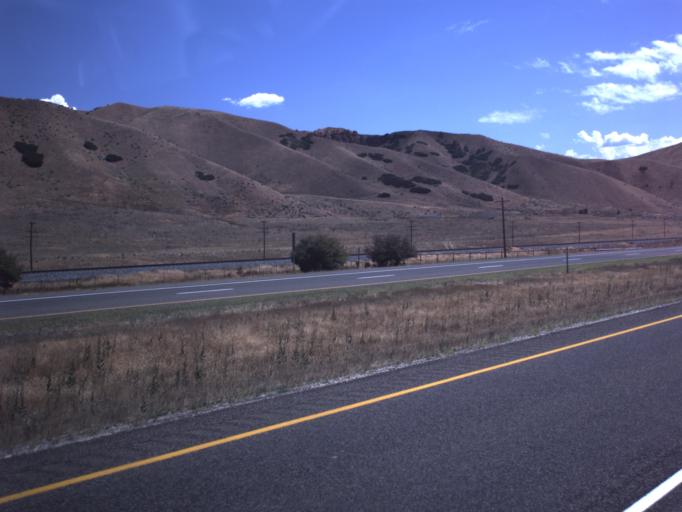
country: US
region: Utah
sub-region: Summit County
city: Coalville
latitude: 40.9896
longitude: -111.4554
